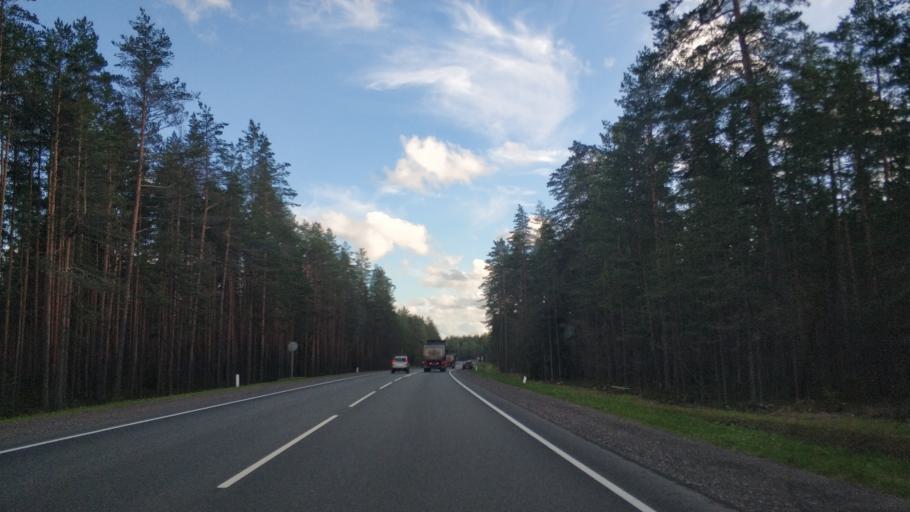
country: RU
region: Leningrad
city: Priozersk
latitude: 60.8851
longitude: 30.1608
